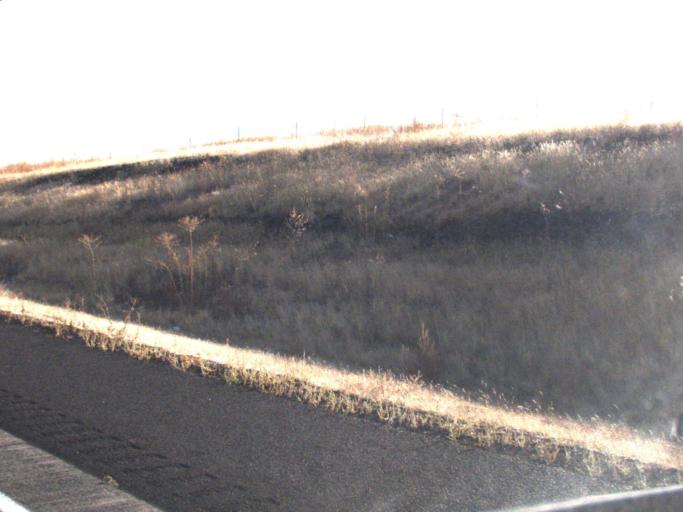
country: US
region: Washington
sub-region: Franklin County
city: Connell
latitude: 46.6264
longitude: -118.8876
